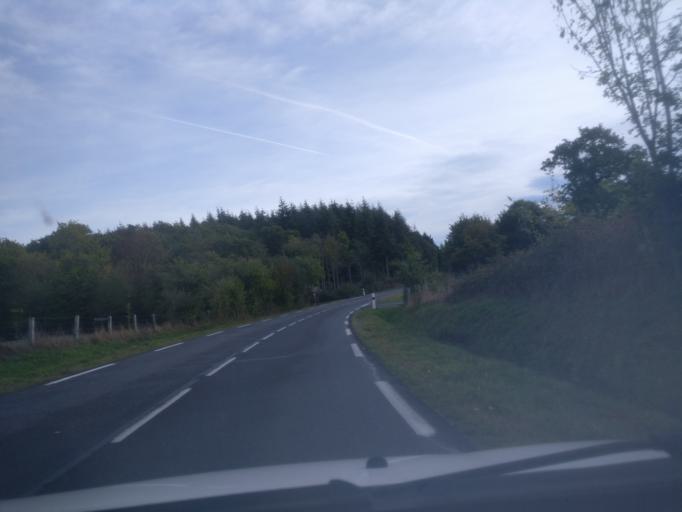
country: FR
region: Lower Normandy
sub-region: Departement de la Manche
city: Jullouville
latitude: 48.7485
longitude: -1.5404
